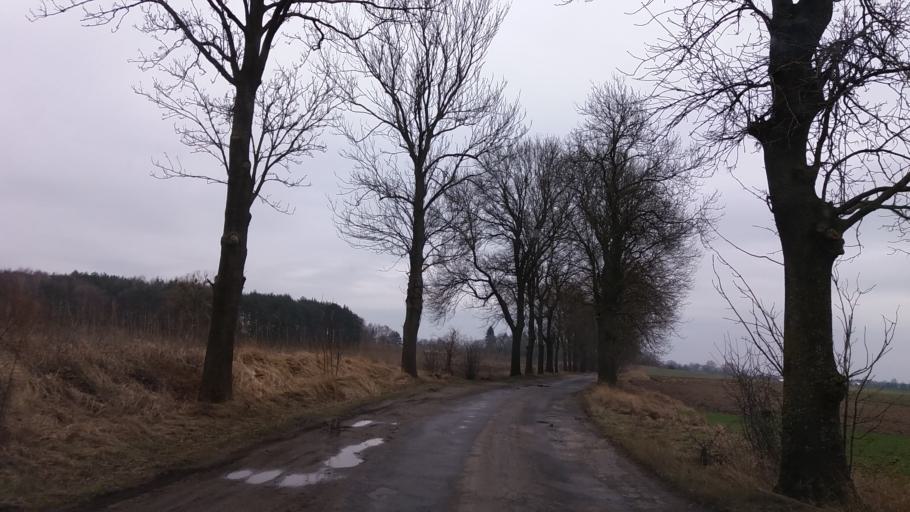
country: PL
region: Lubusz
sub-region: Powiat strzelecko-drezdenecki
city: Dobiegniew
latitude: 53.0269
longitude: 15.7354
